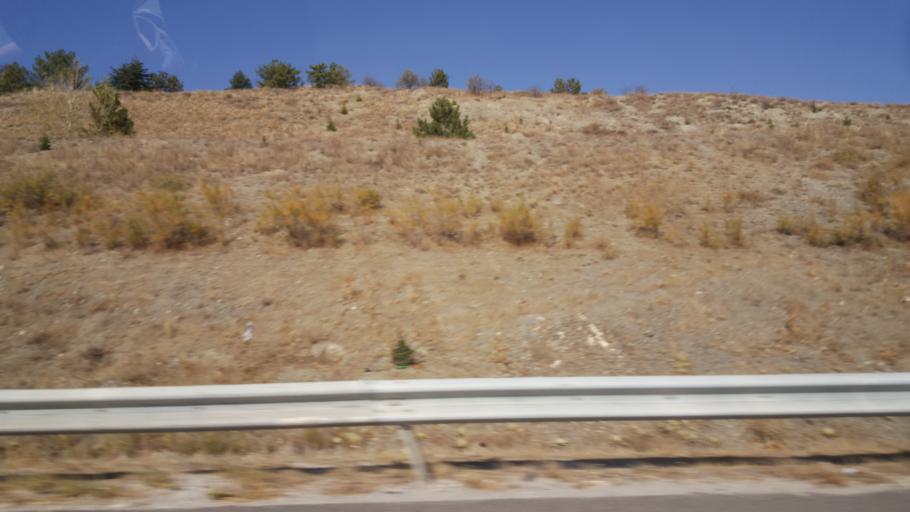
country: TR
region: Ankara
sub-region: Goelbasi
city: Golbasi
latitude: 39.8144
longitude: 32.8134
